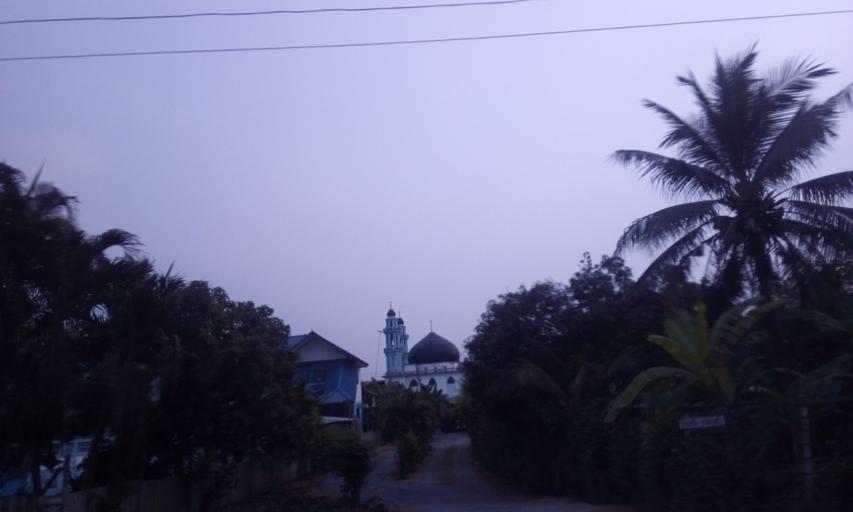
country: TH
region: Bangkok
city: Nong Chok
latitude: 13.8571
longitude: 100.8697
